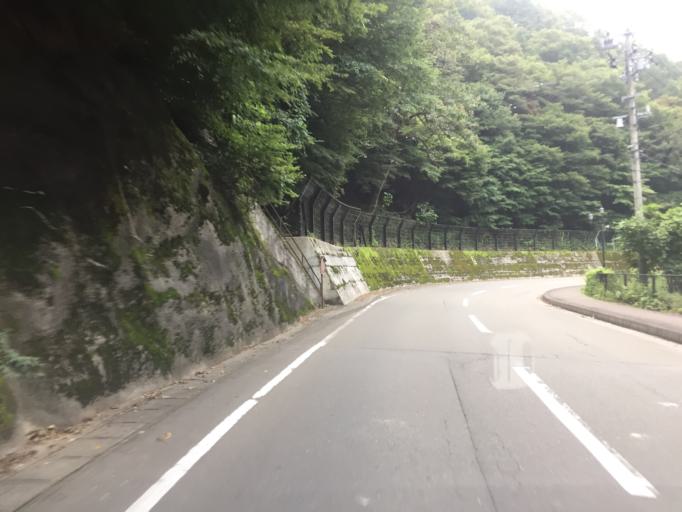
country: JP
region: Fukushima
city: Inawashiro
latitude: 37.4728
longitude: 139.9632
